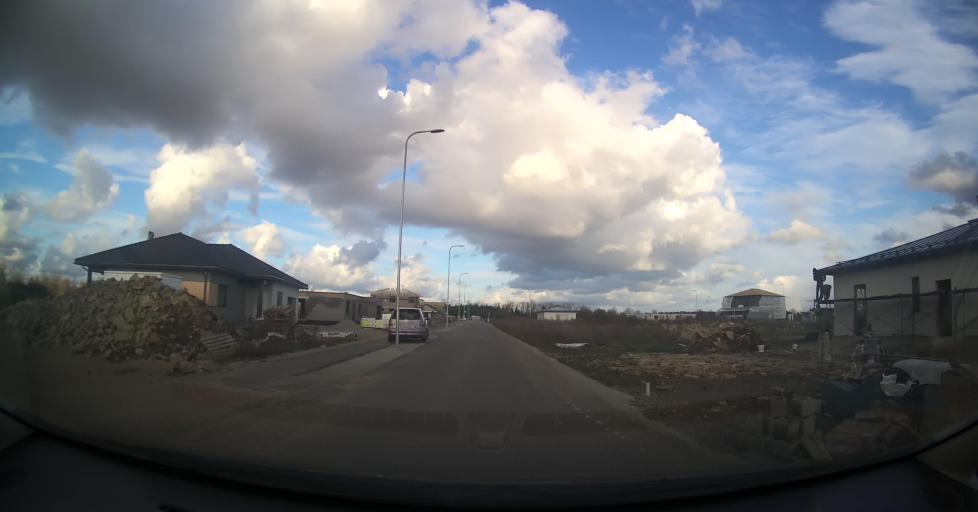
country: EE
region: Harju
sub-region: Joelaehtme vald
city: Loo
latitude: 59.4433
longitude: 24.9643
